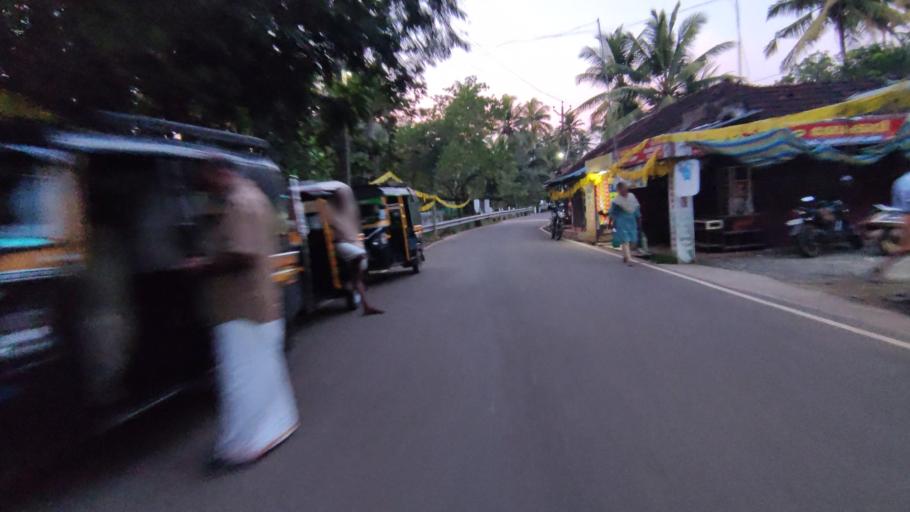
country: IN
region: Kerala
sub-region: Kottayam
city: Kottayam
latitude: 9.5827
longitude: 76.4361
